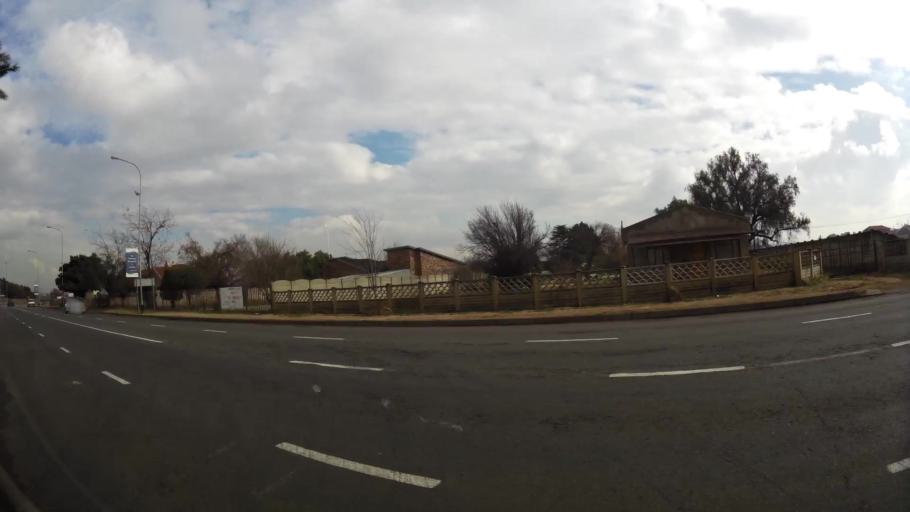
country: ZA
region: Gauteng
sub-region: Sedibeng District Municipality
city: Meyerton
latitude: -26.5955
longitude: 27.9922
